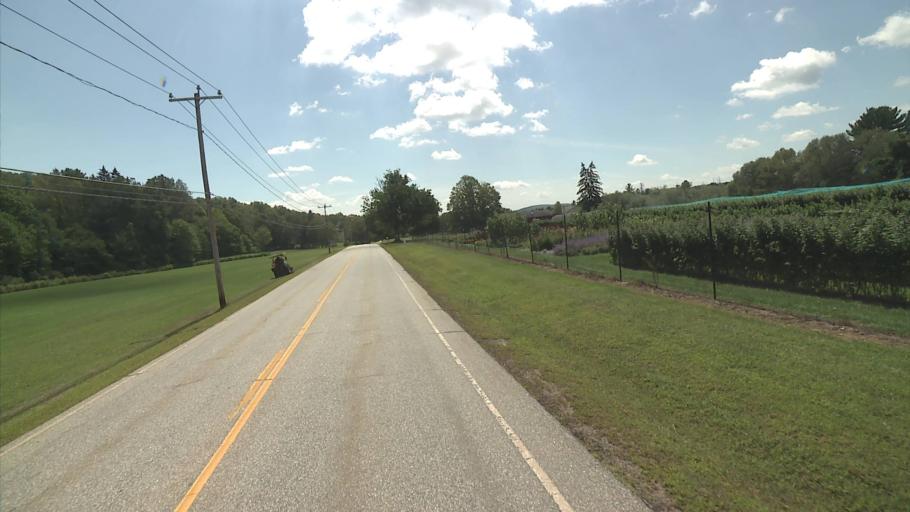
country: US
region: Connecticut
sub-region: Windham County
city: Windham
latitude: 41.7225
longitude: -72.1670
